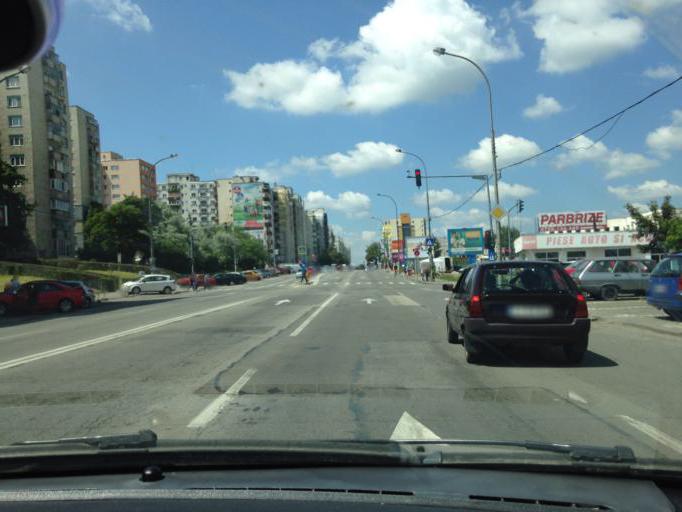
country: RO
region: Cluj
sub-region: Municipiul Cluj-Napoca
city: Cluj-Napoca
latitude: 46.7595
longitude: 23.5541
